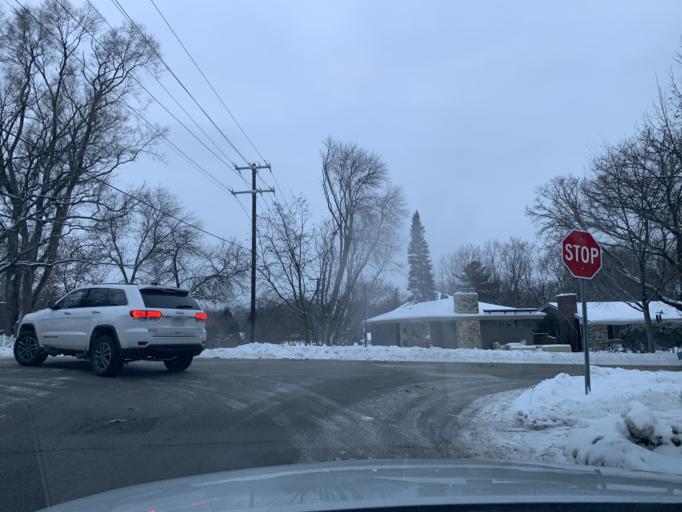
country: US
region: Minnesota
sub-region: Hennepin County
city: Saint Louis Park
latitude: 44.9235
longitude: -93.3407
